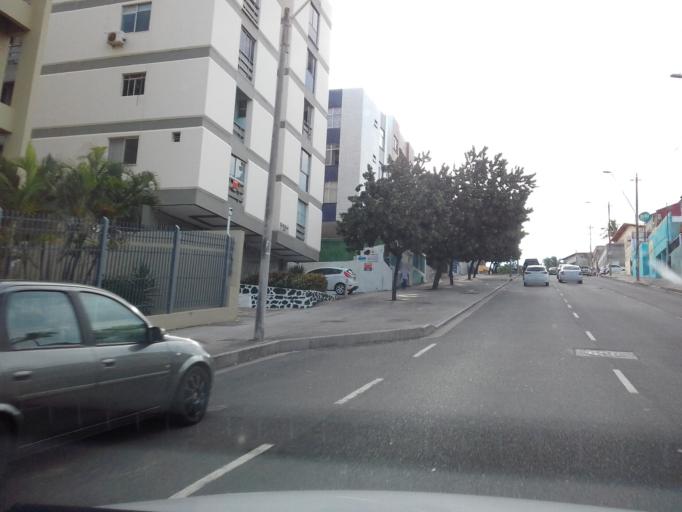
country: BR
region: Bahia
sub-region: Salvador
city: Salvador
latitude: -13.0119
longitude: -38.4718
